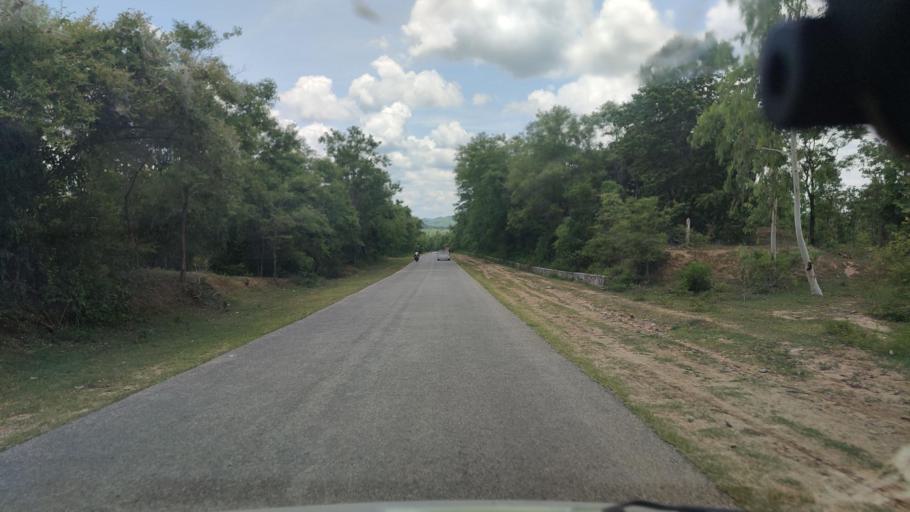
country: MM
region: Magway
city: Taungdwingyi
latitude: 20.1514
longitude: 95.6226
